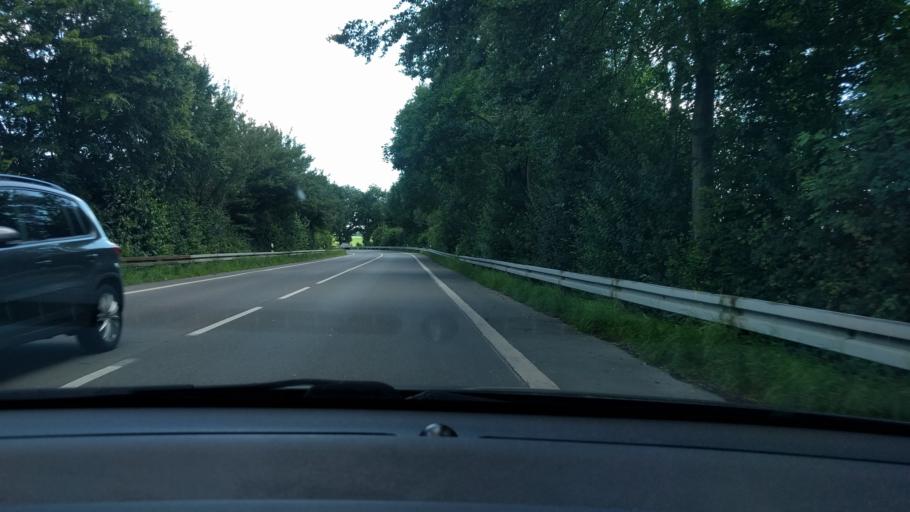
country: DE
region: North Rhine-Westphalia
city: Datteln
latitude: 51.6737
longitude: 7.3266
